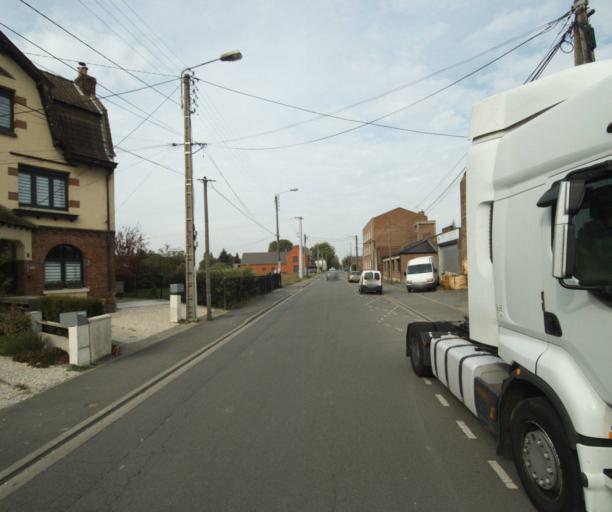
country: FR
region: Nord-Pas-de-Calais
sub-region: Departement du Nord
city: Seclin
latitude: 50.5551
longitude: 3.0280
